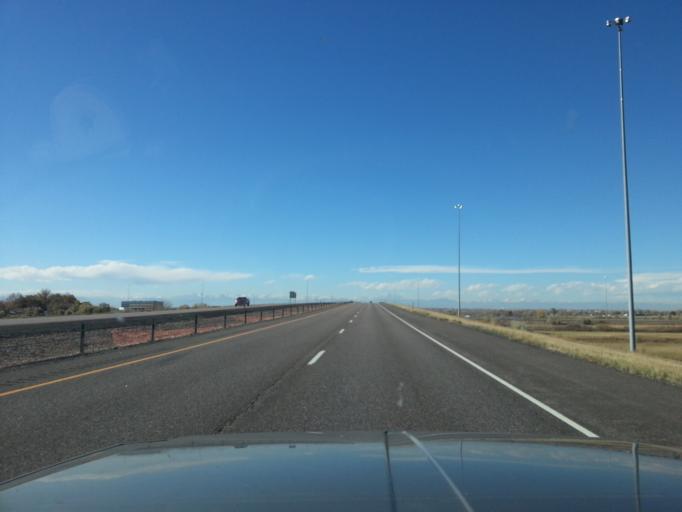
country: US
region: Colorado
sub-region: Adams County
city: Brighton
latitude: 39.9229
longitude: -104.7980
